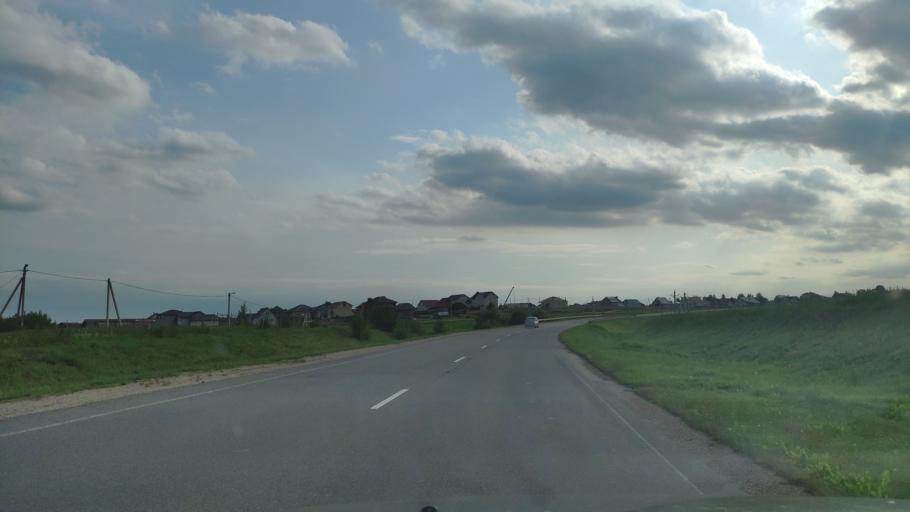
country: BY
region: Minsk
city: Azyartso
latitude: 53.8327
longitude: 27.3219
